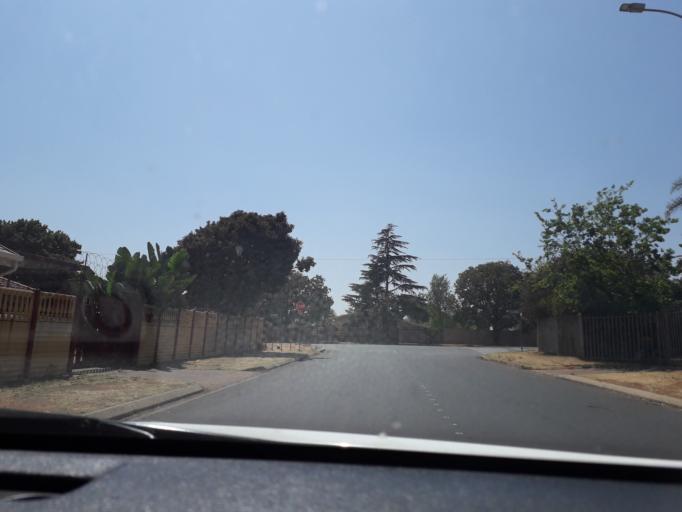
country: ZA
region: Gauteng
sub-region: City of Johannesburg Metropolitan Municipality
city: Modderfontein
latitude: -26.0655
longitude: 28.2067
